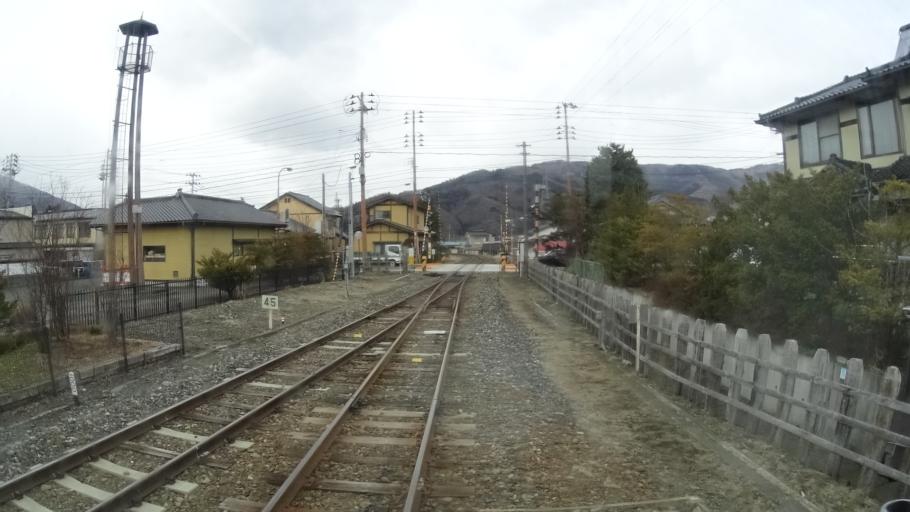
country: JP
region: Iwate
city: Tono
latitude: 39.3332
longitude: 141.5287
